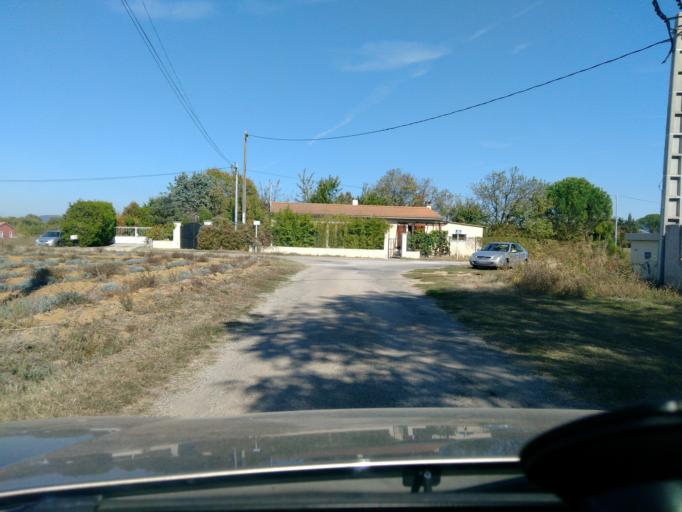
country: FR
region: Rhone-Alpes
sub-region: Departement de la Drome
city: Montboucher-sur-Jabron
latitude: 44.5561
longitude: 4.7886
